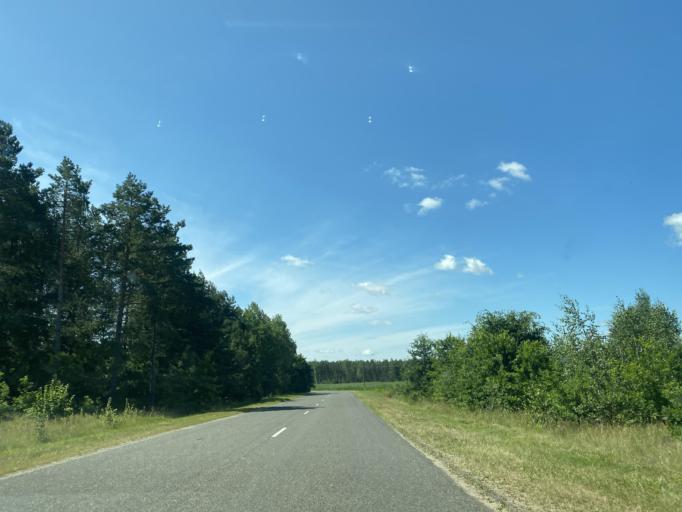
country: BY
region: Brest
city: Ivanava
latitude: 52.2228
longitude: 25.6330
